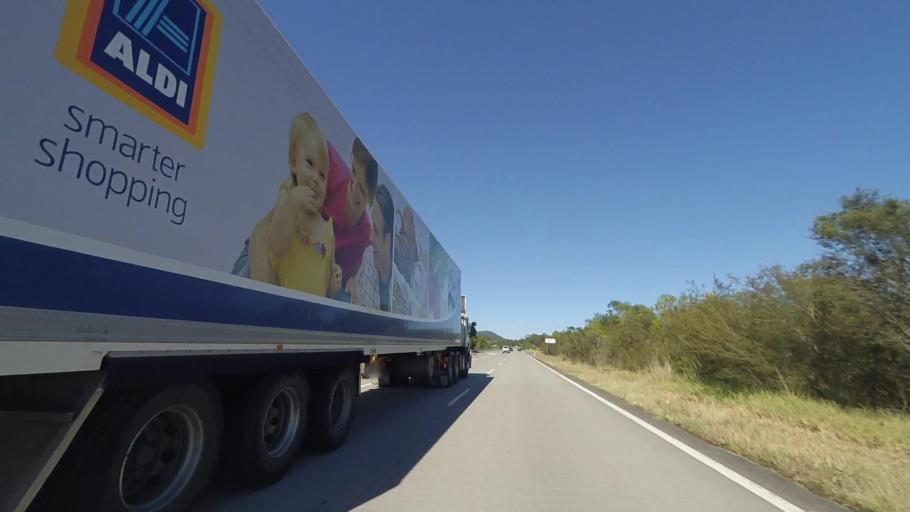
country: AU
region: New South Wales
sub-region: Port Stephens Shire
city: Port Stephens
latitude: -32.6236
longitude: 152.0617
